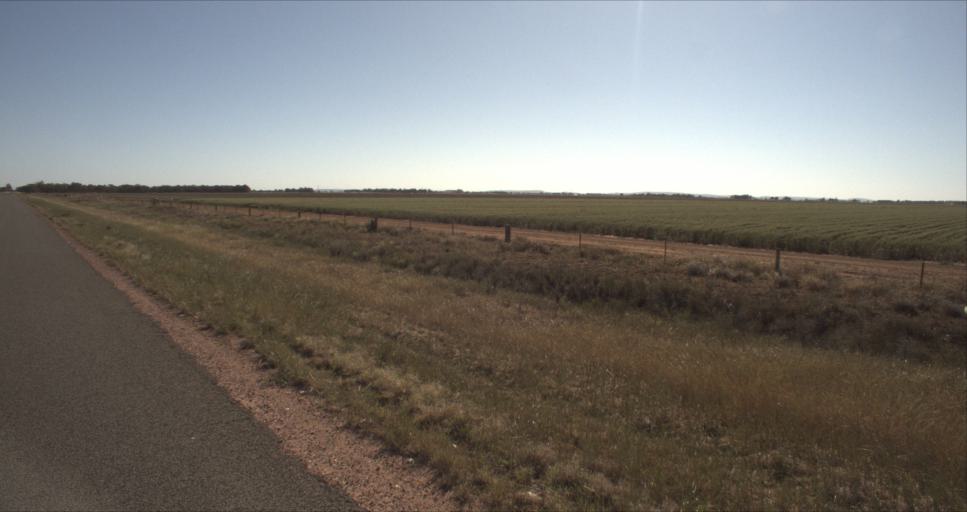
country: AU
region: New South Wales
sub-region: Leeton
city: Leeton
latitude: -34.5737
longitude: 146.2630
